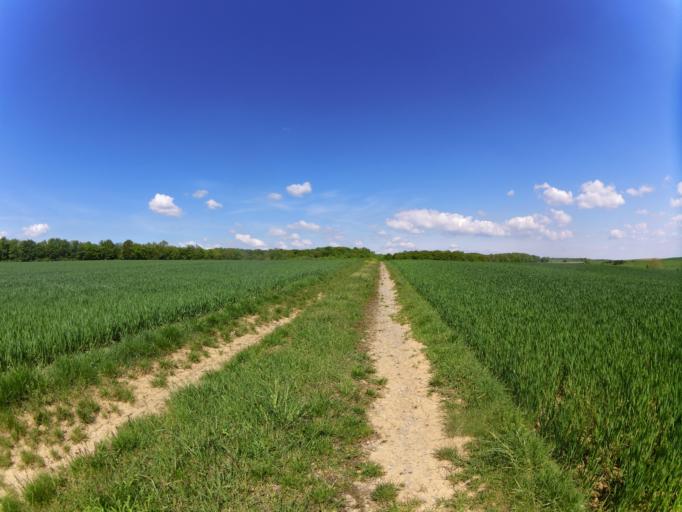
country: DE
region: Bavaria
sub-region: Regierungsbezirk Unterfranken
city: Rimpar
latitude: 49.8751
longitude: 9.9962
